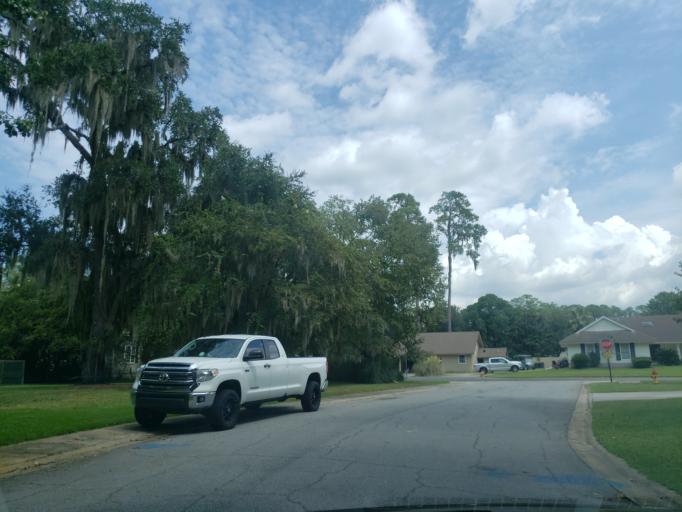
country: US
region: Georgia
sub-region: Chatham County
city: Isle of Hope
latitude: 31.9878
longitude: -81.0494
